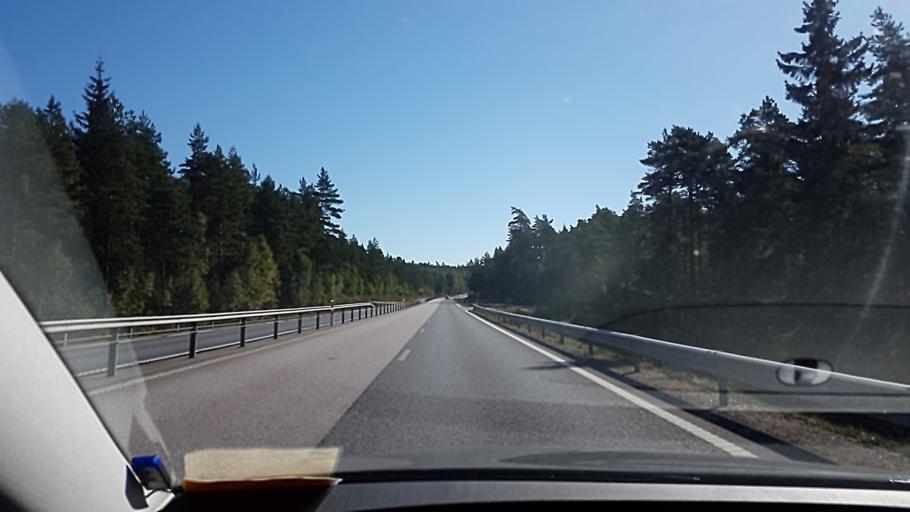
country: SE
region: Kronoberg
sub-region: Vaxjo Kommun
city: Vaexjoe
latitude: 56.8762
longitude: 14.9197
